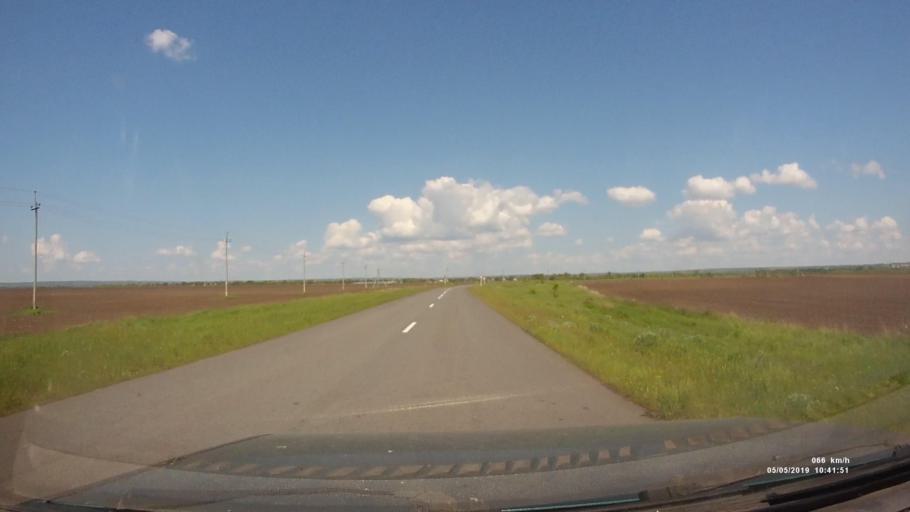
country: RU
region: Rostov
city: Ust'-Donetskiy
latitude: 47.5939
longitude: 40.8387
